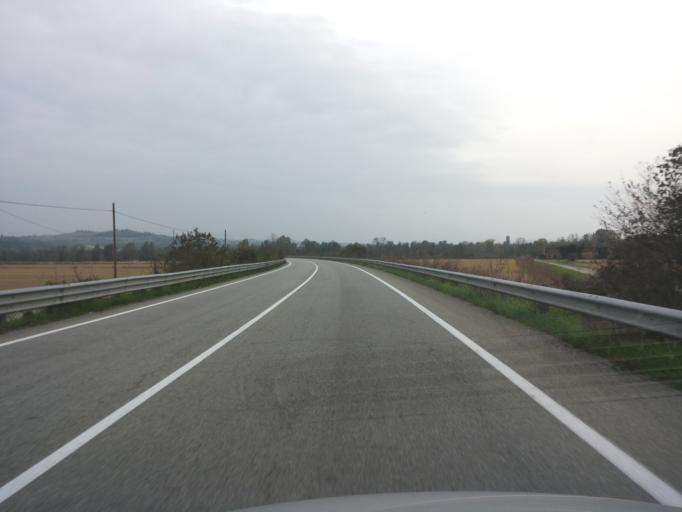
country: IT
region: Piedmont
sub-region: Provincia di Alessandria
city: Pontestura
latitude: 45.1576
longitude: 8.3322
